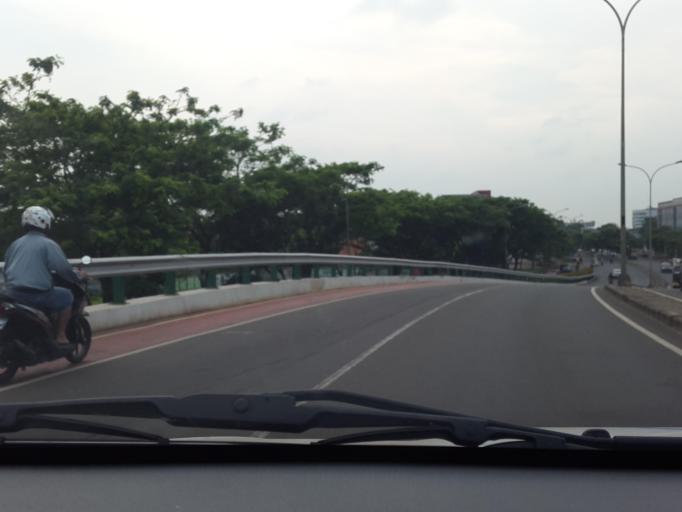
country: ID
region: Banten
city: South Tangerang
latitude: -6.2754
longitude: 106.7060
